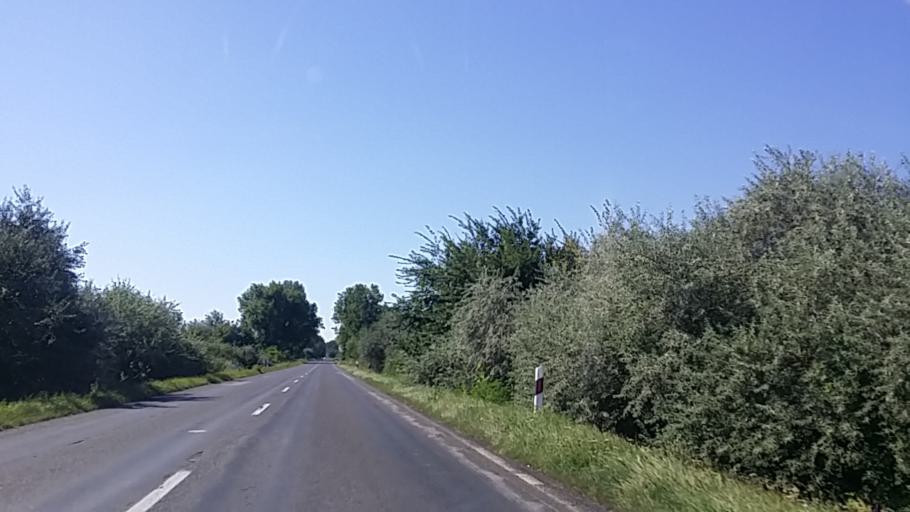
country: HU
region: Fejer
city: Cece
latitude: 46.8066
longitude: 18.6392
